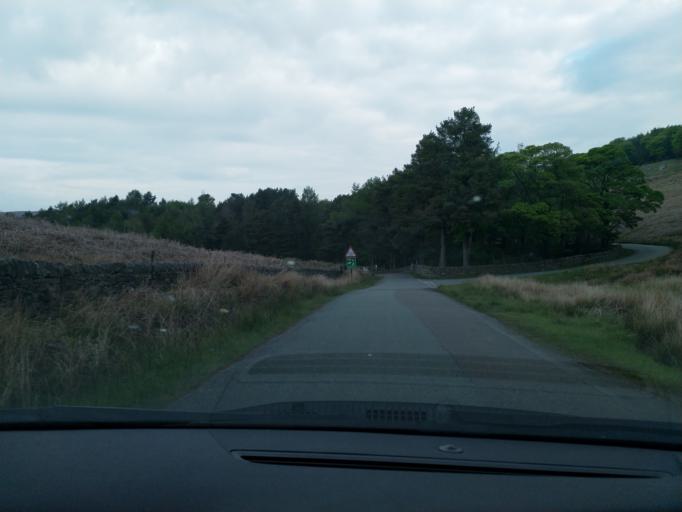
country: GB
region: England
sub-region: Derbyshire
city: Hathersage
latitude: 53.3478
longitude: -1.6403
